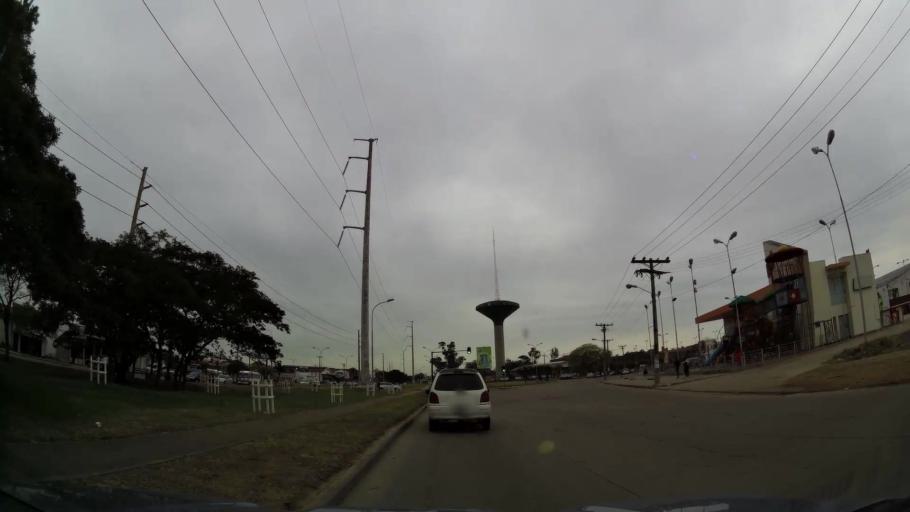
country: BO
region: Santa Cruz
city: Santa Cruz de la Sierra
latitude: -17.7662
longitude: -63.1482
